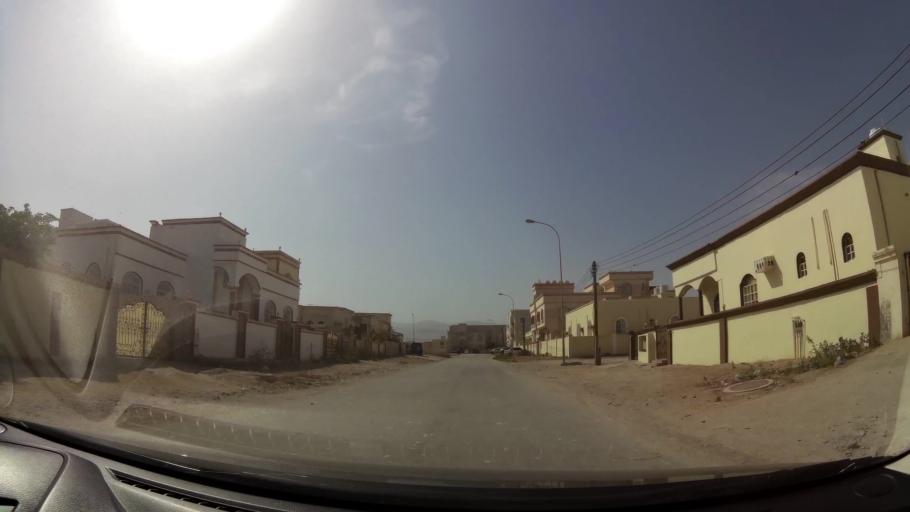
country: OM
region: Zufar
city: Salalah
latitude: 17.0029
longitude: 54.0157
